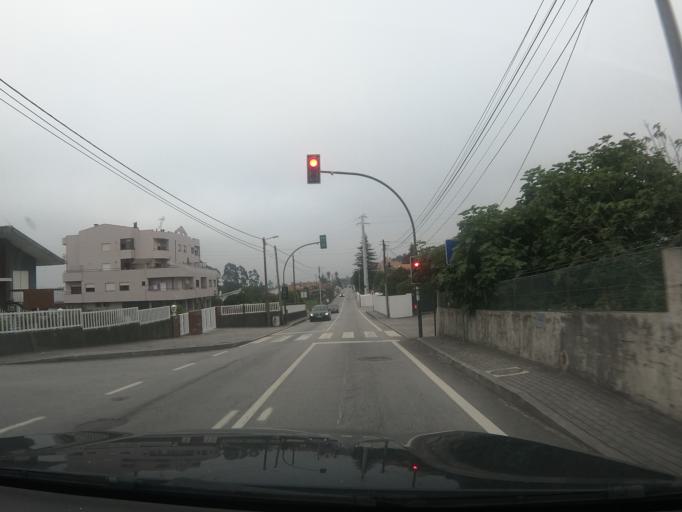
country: PT
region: Aveiro
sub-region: Santa Maria da Feira
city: Lamas
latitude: 41.0085
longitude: -8.5601
